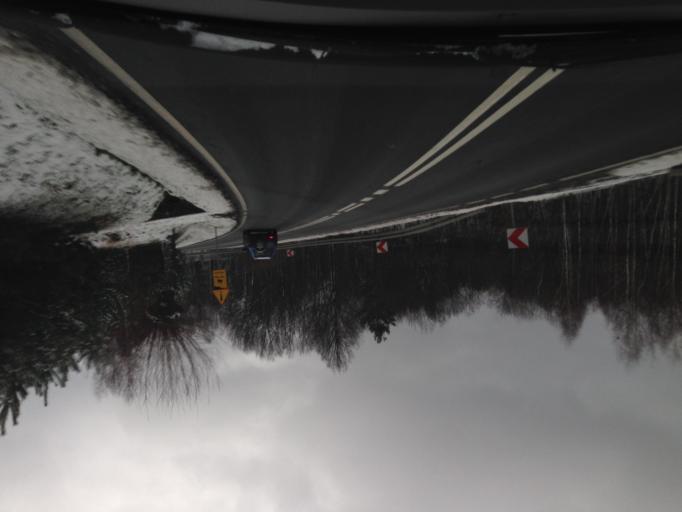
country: PL
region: Lesser Poland Voivodeship
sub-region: Powiat tarnowski
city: Siemiechow
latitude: 49.8471
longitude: 20.9319
